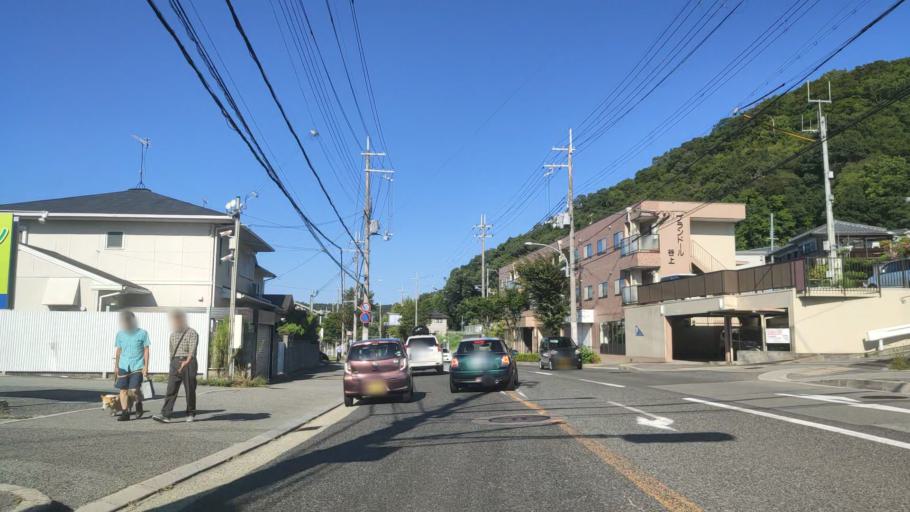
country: JP
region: Hyogo
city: Kobe
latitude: 34.7614
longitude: 135.1630
